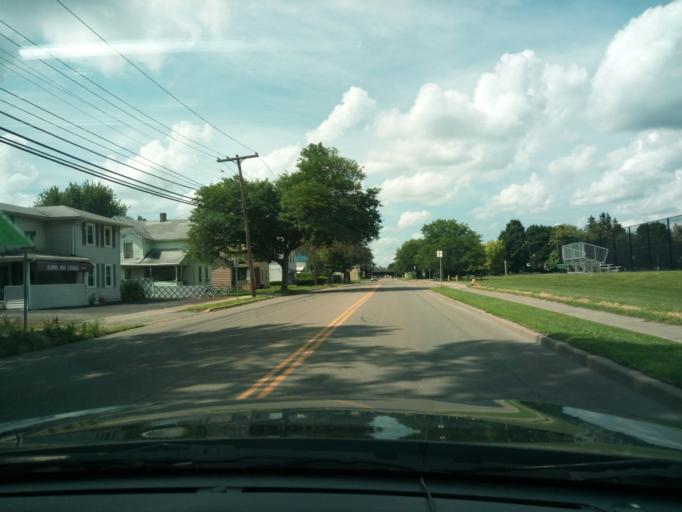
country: US
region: New York
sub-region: Chemung County
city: Elmira
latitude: 42.0705
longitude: -76.7990
